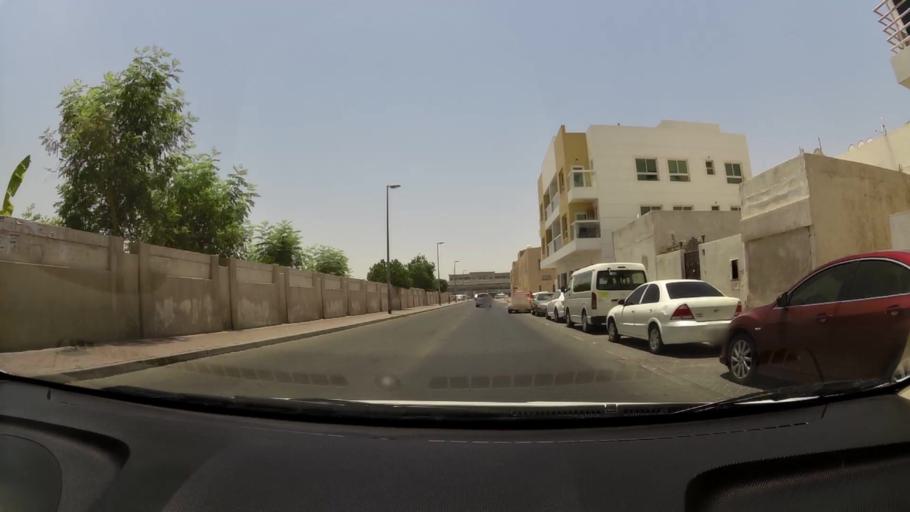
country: AE
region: Ash Shariqah
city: Sharjah
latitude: 25.2750
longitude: 55.3383
